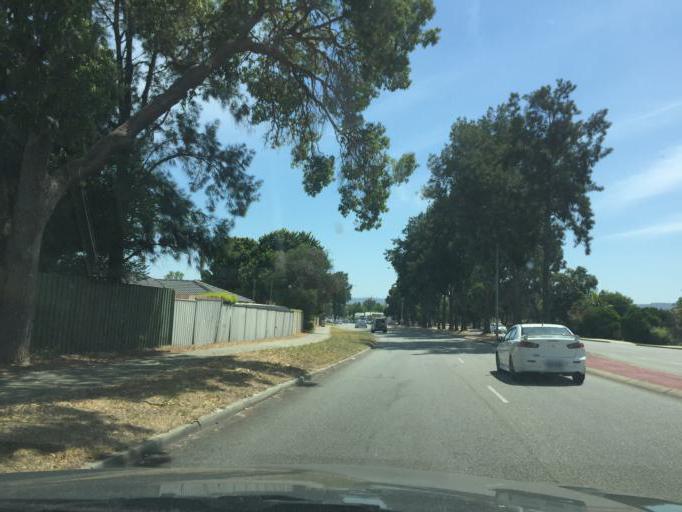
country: AU
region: Western Australia
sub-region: Gosnells
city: Thornlie
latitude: -32.0697
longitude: 115.9681
